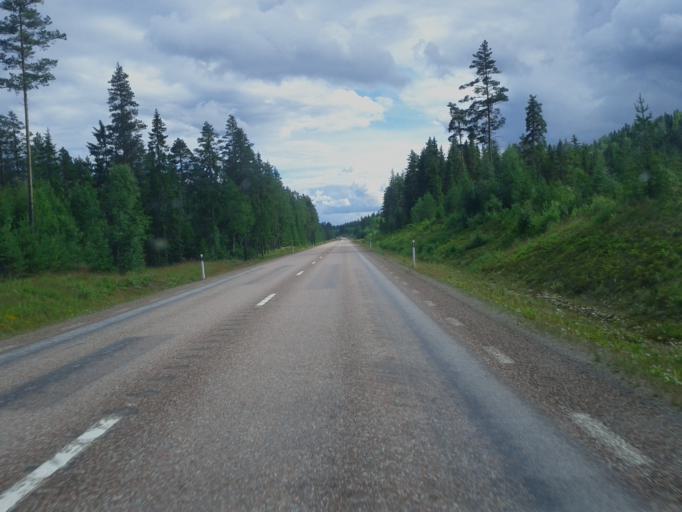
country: SE
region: Dalarna
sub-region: Rattviks Kommun
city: Raettvik
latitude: 60.8120
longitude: 15.2606
